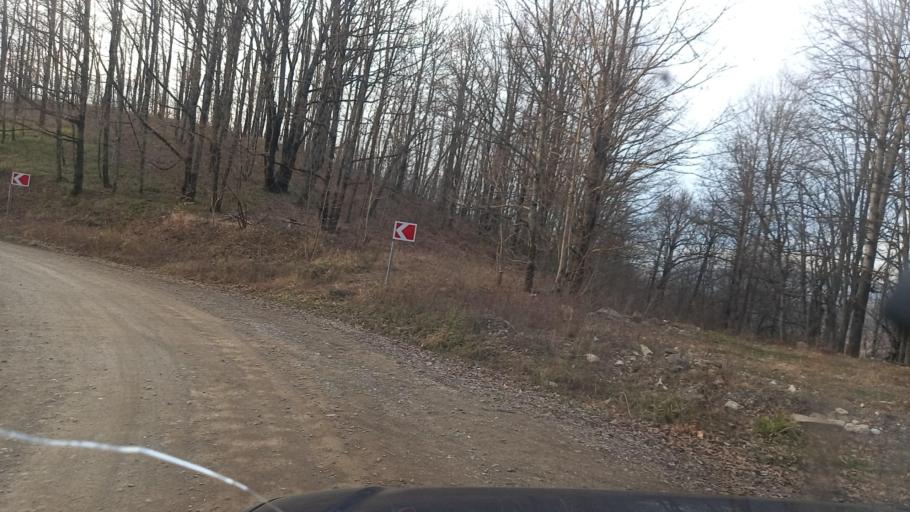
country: RU
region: Krasnodarskiy
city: Goryachiy Klyuch
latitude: 44.3693
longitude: 39.2201
